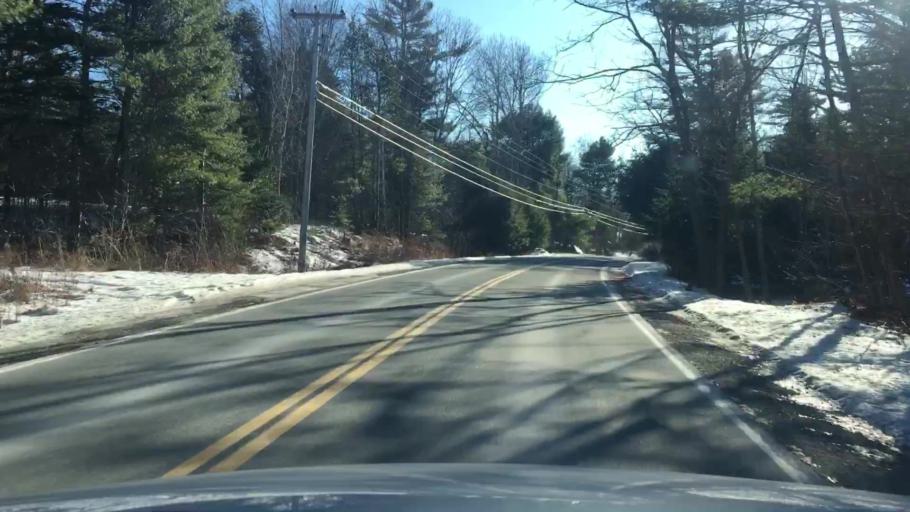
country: US
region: Maine
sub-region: Hancock County
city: Orland
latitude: 44.5457
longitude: -68.7433
